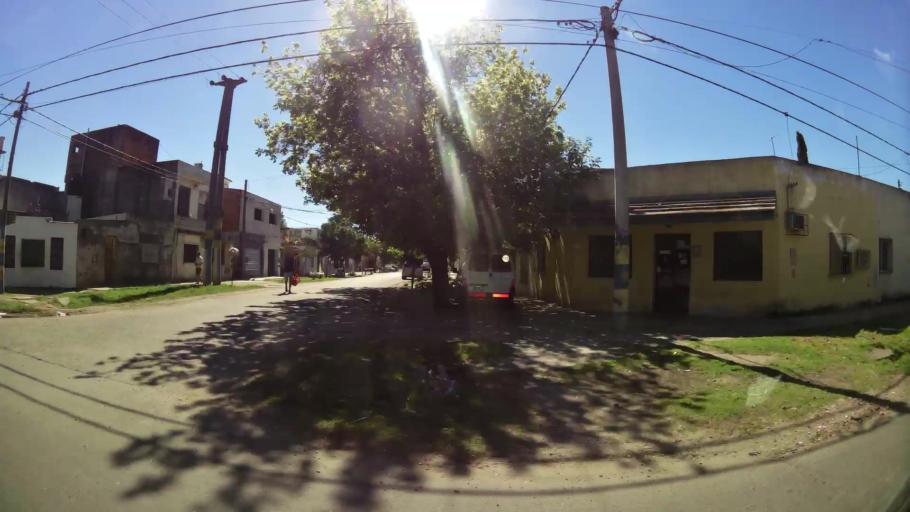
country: AR
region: Santa Fe
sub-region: Departamento de Rosario
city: Rosario
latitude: -32.9637
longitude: -60.6963
